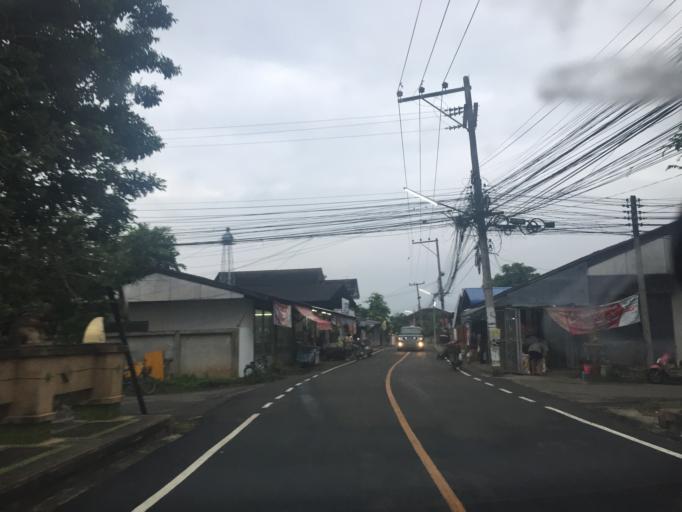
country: TH
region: Lamphun
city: Ban Thi
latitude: 18.6435
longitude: 99.0473
